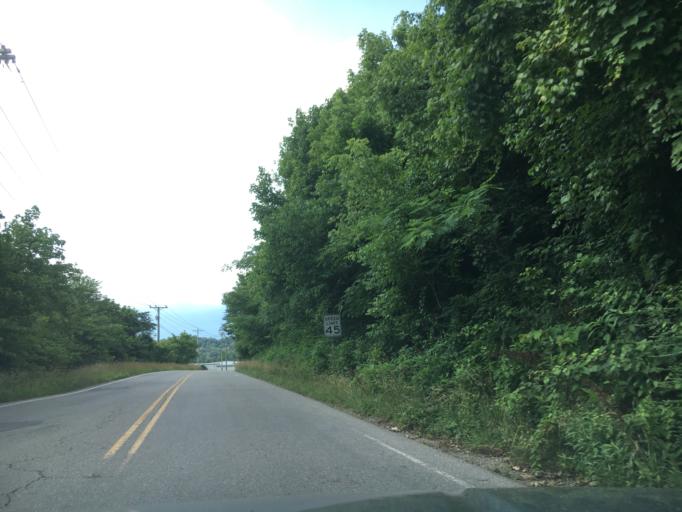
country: US
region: Virginia
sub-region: Roanoke County
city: Cave Spring
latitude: 37.1936
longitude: -79.9993
